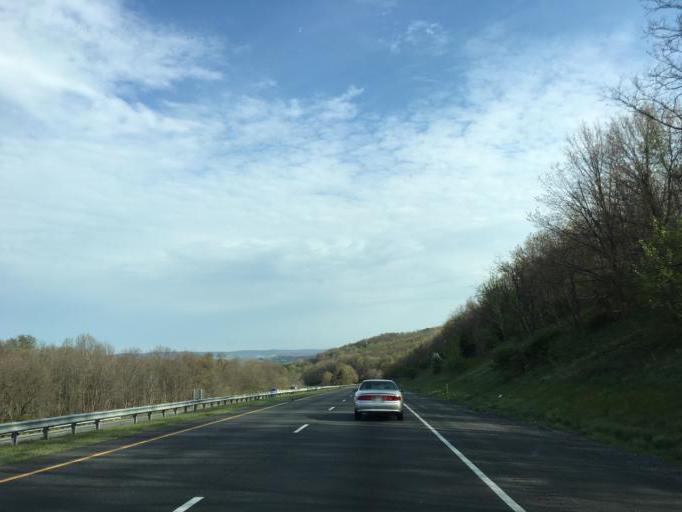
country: US
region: Maryland
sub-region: Frederick County
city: Braddock Heights
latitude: 39.4488
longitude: -77.5034
